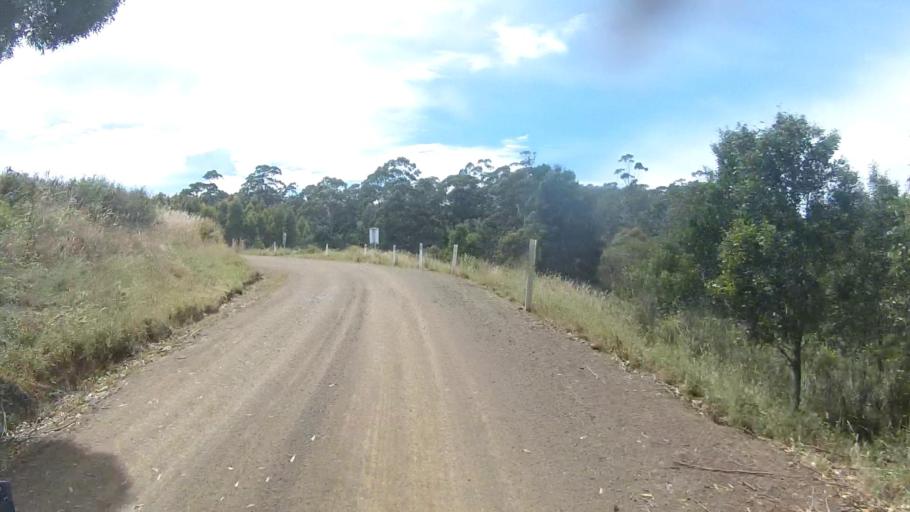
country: AU
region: Tasmania
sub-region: Sorell
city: Sorell
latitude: -42.7865
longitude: 147.8425
